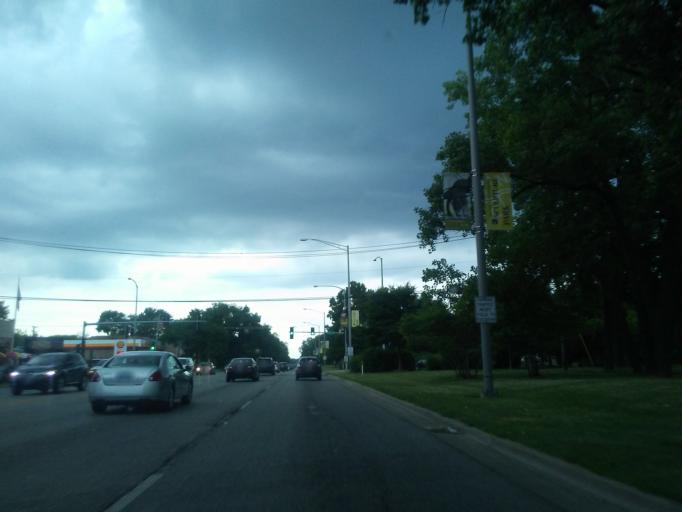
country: US
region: Illinois
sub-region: Cook County
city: Evanston
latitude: 42.0329
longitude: -87.7109
